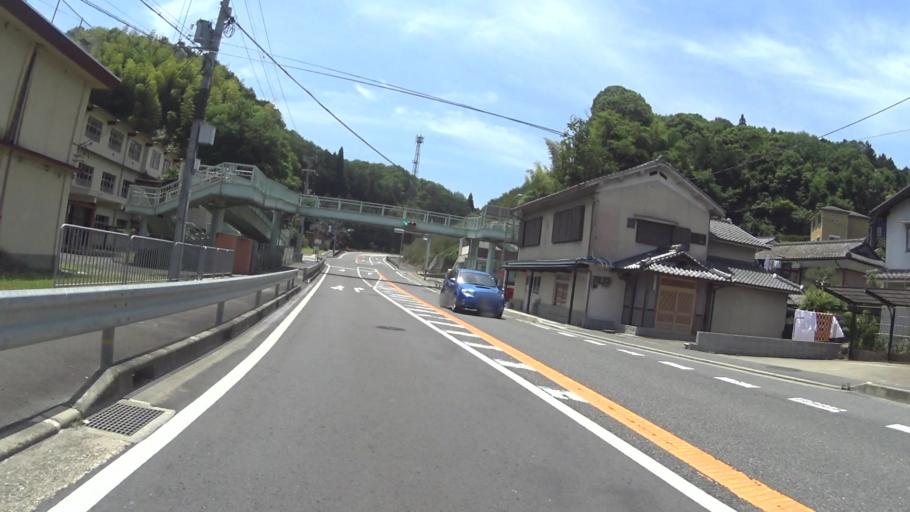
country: JP
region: Kyoto
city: Ayabe
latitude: 35.1887
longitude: 135.3244
